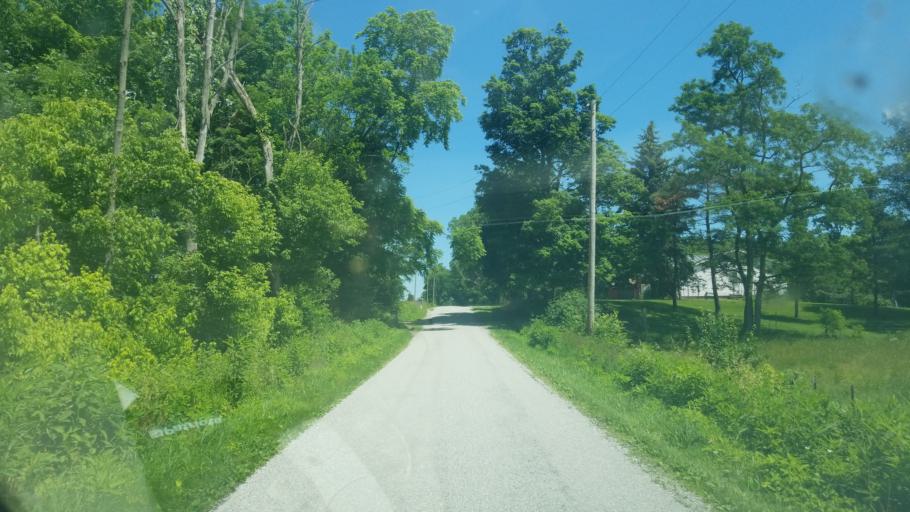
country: US
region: Ohio
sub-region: Huron County
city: New London
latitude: 41.1552
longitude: -82.3896
